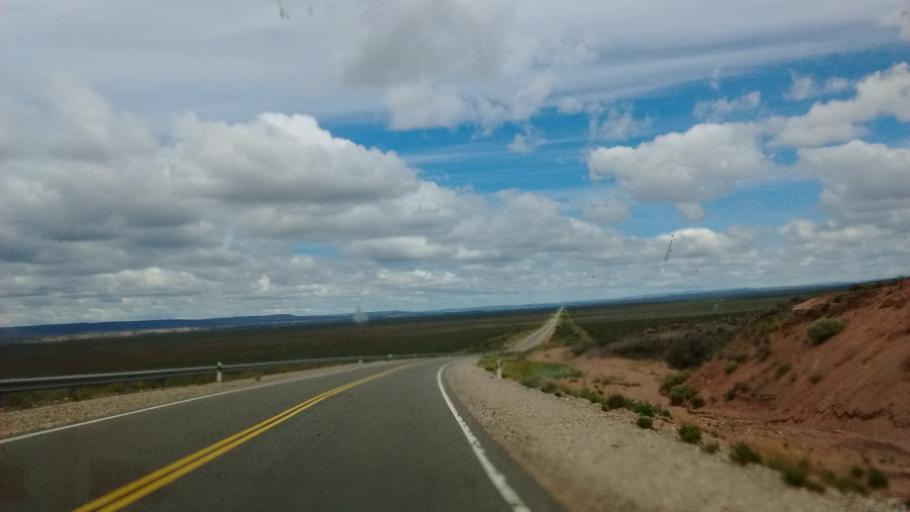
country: AR
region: Neuquen
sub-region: Departamento de Picun Leufu
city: Picun Leufu
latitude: -39.7830
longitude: -69.6584
